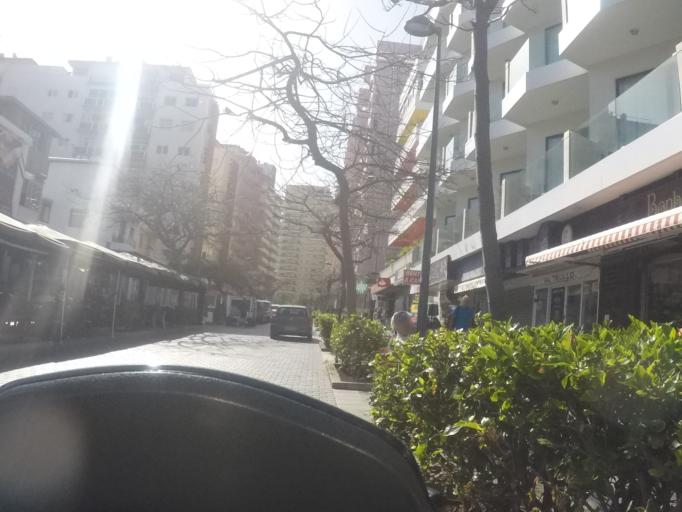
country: ES
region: Canary Islands
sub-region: Provincia de Santa Cruz de Tenerife
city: Puerto de la Cruz
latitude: 28.4182
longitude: -16.5441
